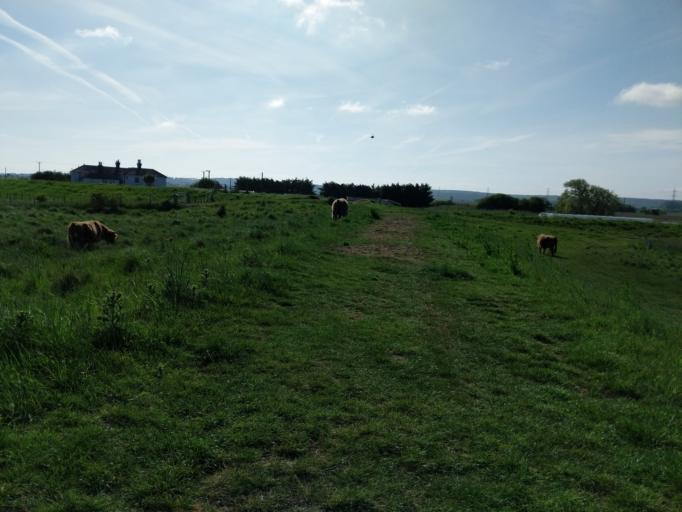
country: GB
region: England
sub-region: Kent
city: Dunkirk
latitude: 51.3439
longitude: 0.9566
